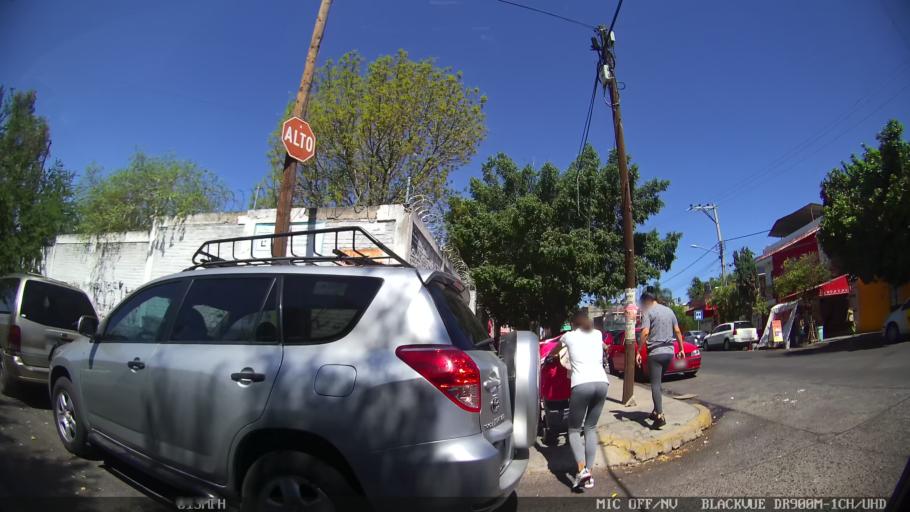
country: MX
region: Jalisco
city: Tlaquepaque
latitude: 20.6944
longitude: -103.2938
